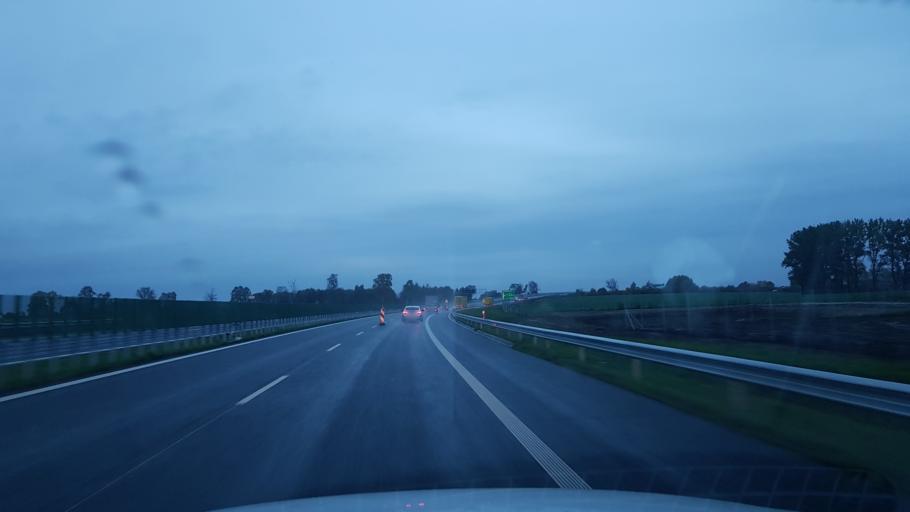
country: PL
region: West Pomeranian Voivodeship
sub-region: Powiat gryficki
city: Ploty
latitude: 53.8075
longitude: 15.2481
